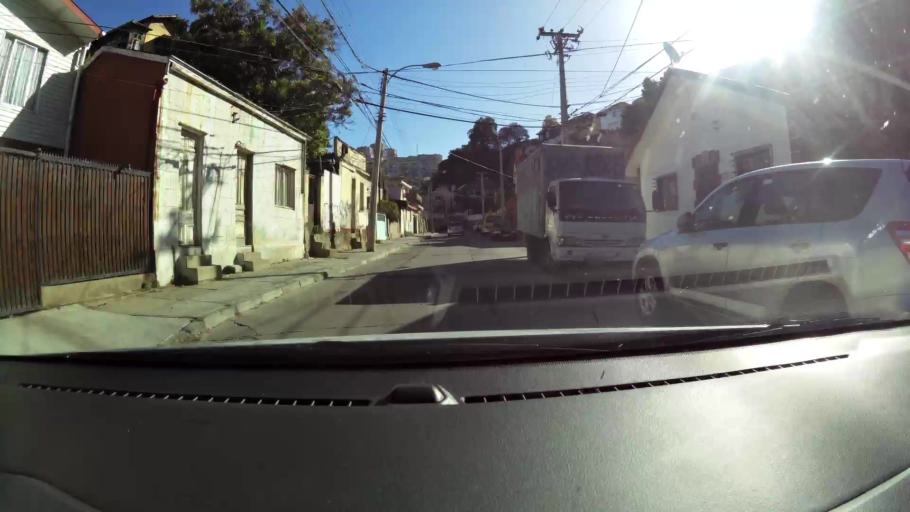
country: CL
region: Valparaiso
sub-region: Provincia de Valparaiso
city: Vina del Mar
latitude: -33.0309
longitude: -71.5625
